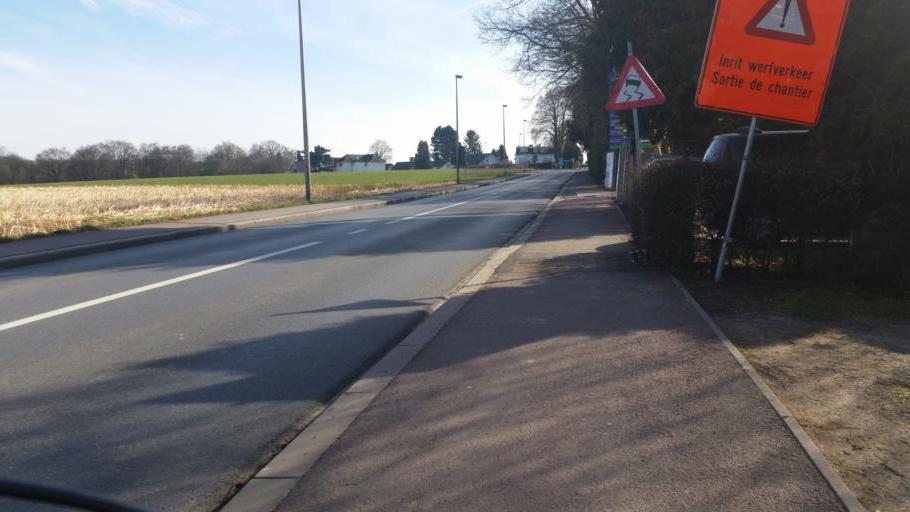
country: BE
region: Flanders
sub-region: Provincie Vlaams-Brabant
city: Wezembeek-Oppem
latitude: 50.8338
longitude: 4.5000
